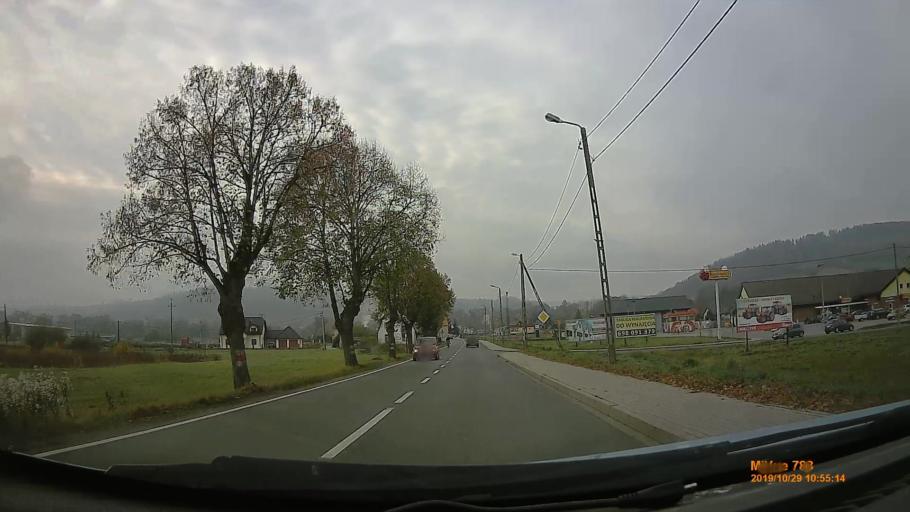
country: PL
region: Lower Silesian Voivodeship
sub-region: Powiat klodzki
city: Nowa Ruda
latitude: 50.5206
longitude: 16.4949
